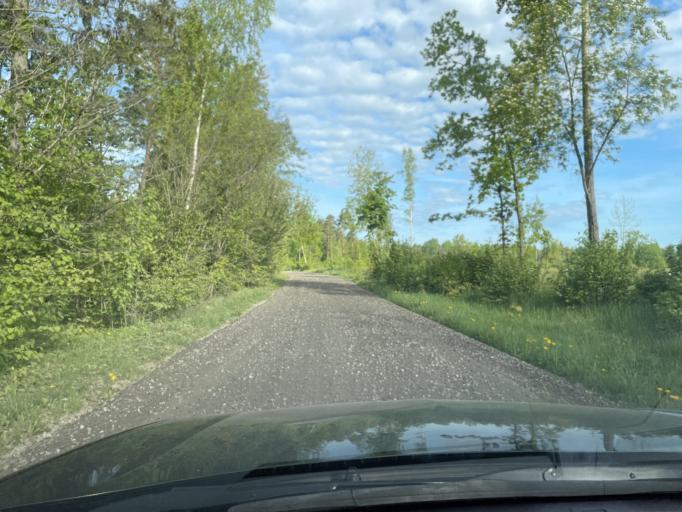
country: EE
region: Harju
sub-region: Keila linn
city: Keila
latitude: 59.3078
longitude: 24.2920
